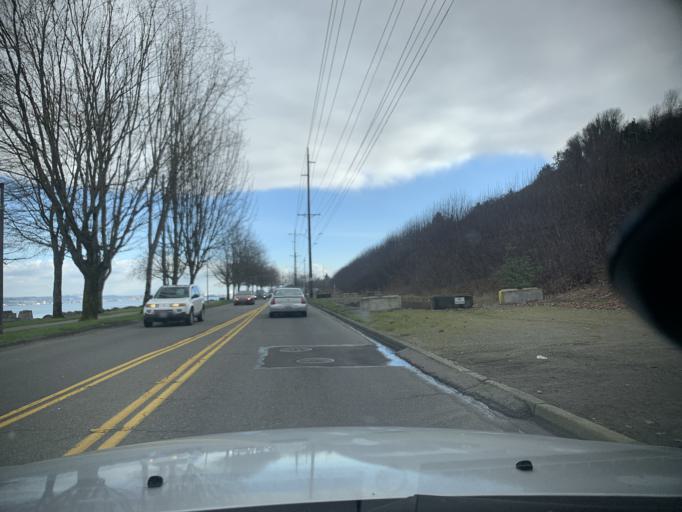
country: US
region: Washington
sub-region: Pierce County
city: Fircrest
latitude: 47.2939
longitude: -122.4980
